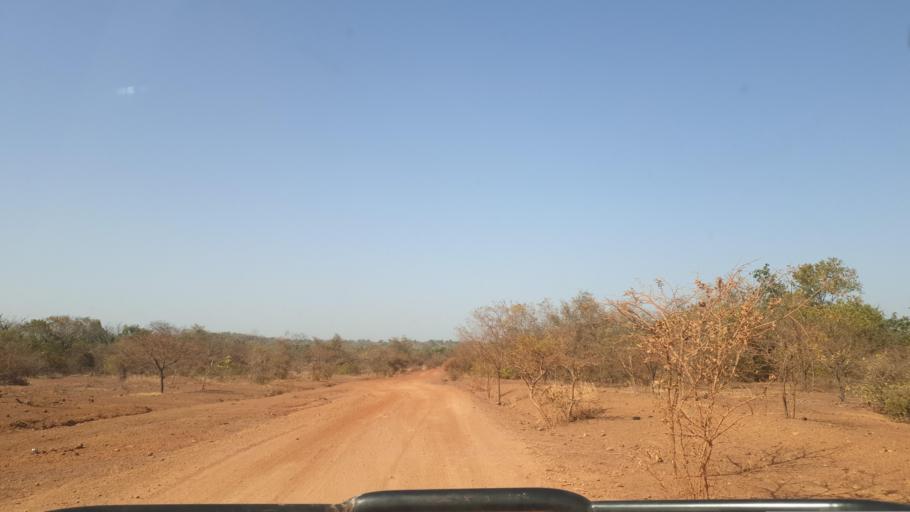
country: ML
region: Sikasso
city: Bougouni
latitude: 11.8209
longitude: -6.9603
